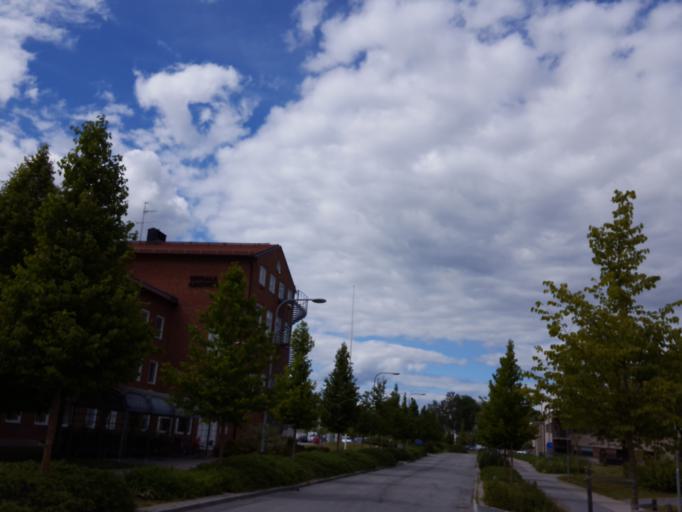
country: SE
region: Uppsala
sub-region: Uppsala Kommun
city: Uppsala
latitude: 59.8483
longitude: 17.6346
